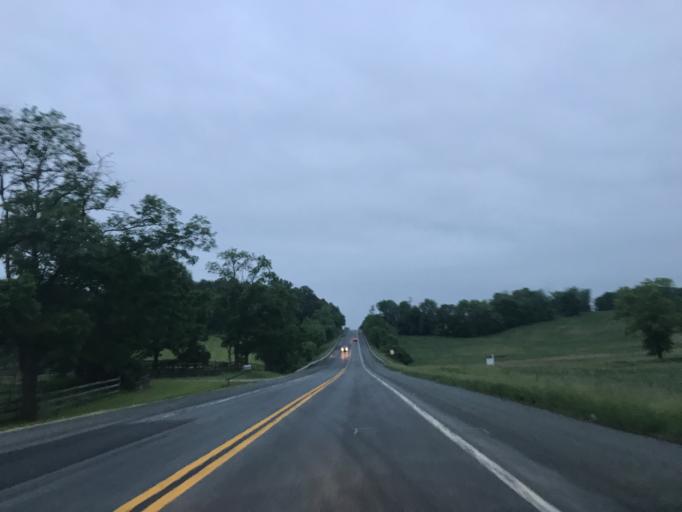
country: US
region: Maryland
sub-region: Frederick County
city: Linganore
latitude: 39.4106
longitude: -77.2557
